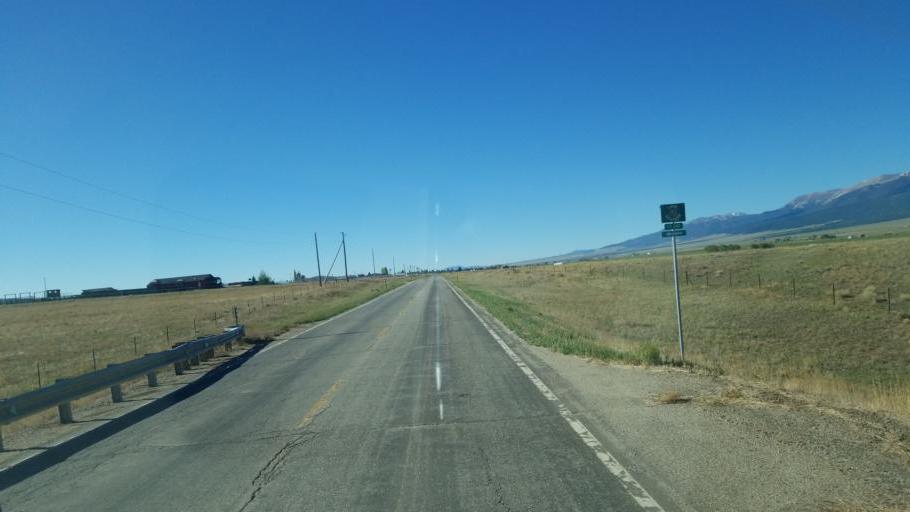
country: US
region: Colorado
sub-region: Custer County
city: Westcliffe
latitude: 38.1564
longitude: -105.4805
